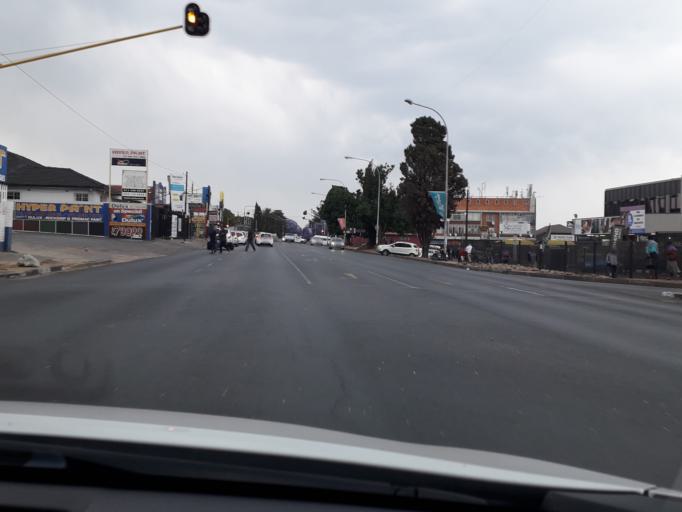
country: ZA
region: Gauteng
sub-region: City of Johannesburg Metropolitan Municipality
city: Johannesburg
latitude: -26.1392
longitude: 28.0883
